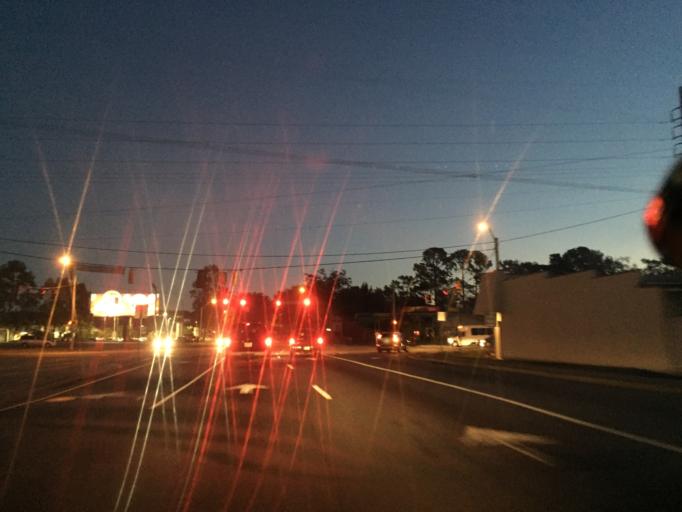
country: US
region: Georgia
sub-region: Chatham County
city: Montgomery
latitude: 31.9978
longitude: -81.1225
